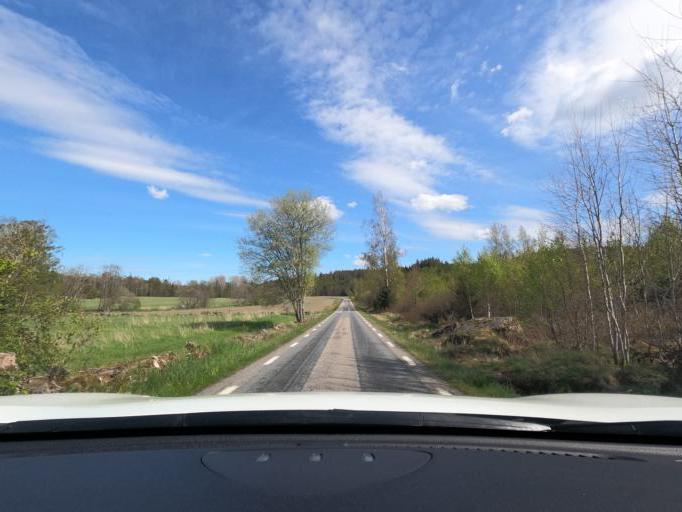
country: SE
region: Vaestra Goetaland
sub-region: Marks Kommun
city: Horred
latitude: 57.4505
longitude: 12.4561
